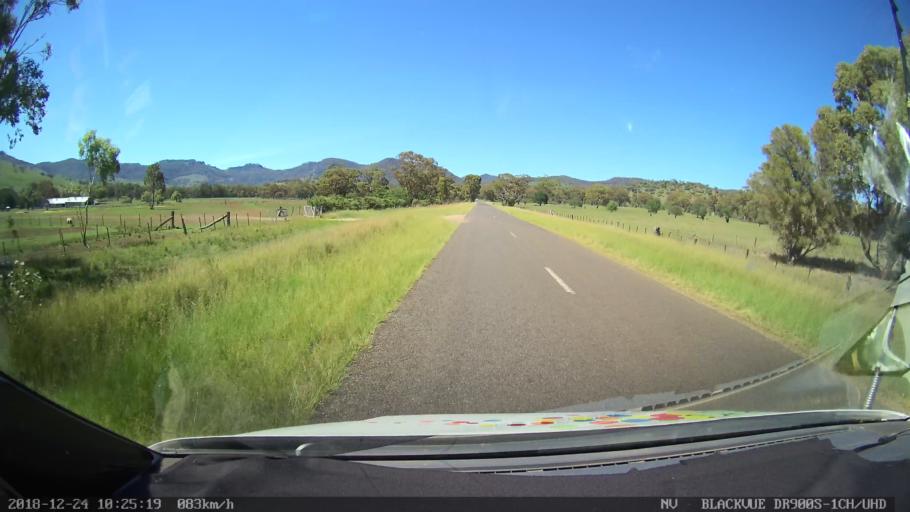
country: AU
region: New South Wales
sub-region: Liverpool Plains
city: Quirindi
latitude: -31.7974
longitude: 150.5290
